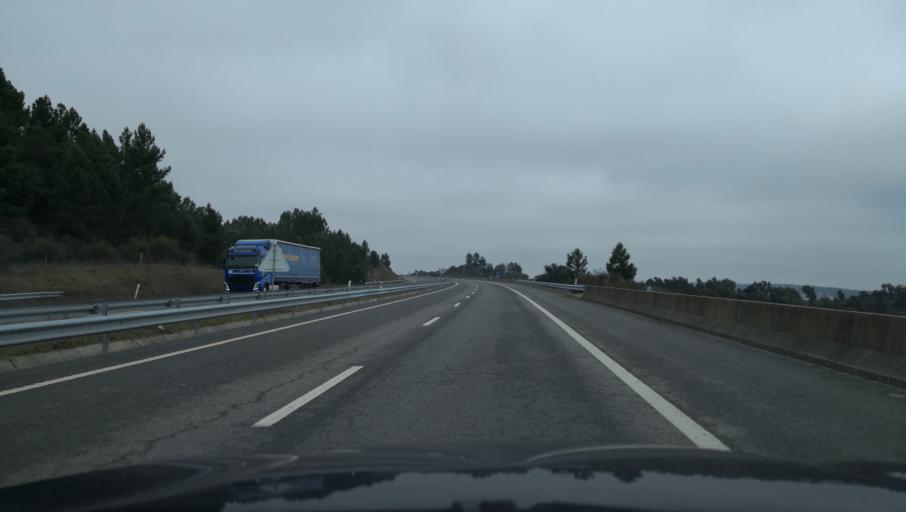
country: PT
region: Vila Real
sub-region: Chaves
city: Chaves
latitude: 41.7034
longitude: -7.5482
